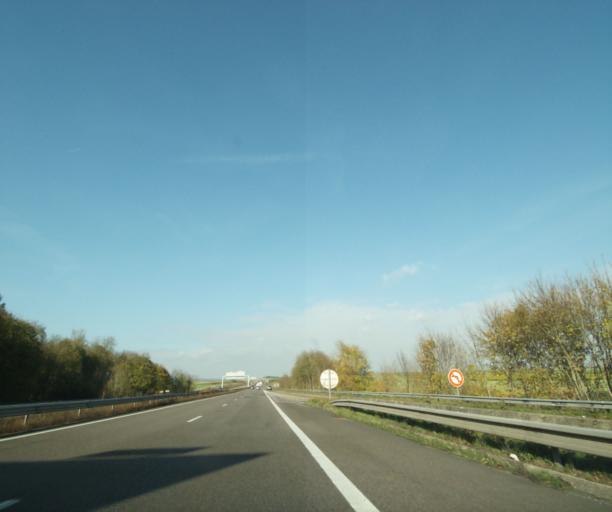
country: FR
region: Champagne-Ardenne
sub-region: Departement de la Marne
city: Fagnieres
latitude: 49.0580
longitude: 4.2839
